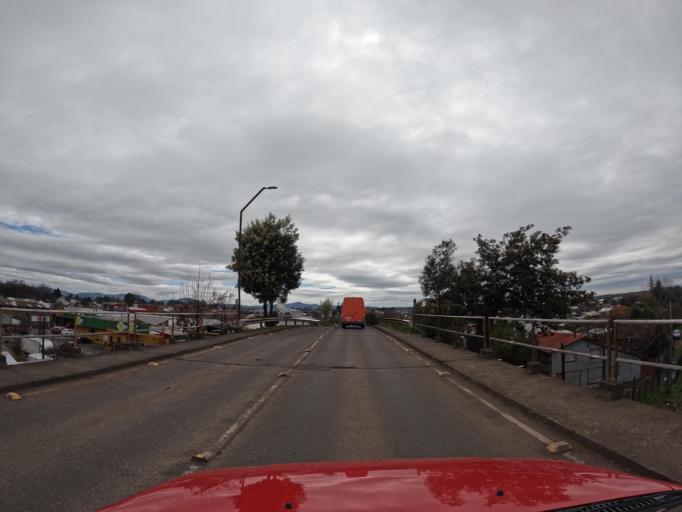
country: CL
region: Araucania
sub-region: Provincia de Malleco
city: Victoria
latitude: -38.2348
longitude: -72.3283
